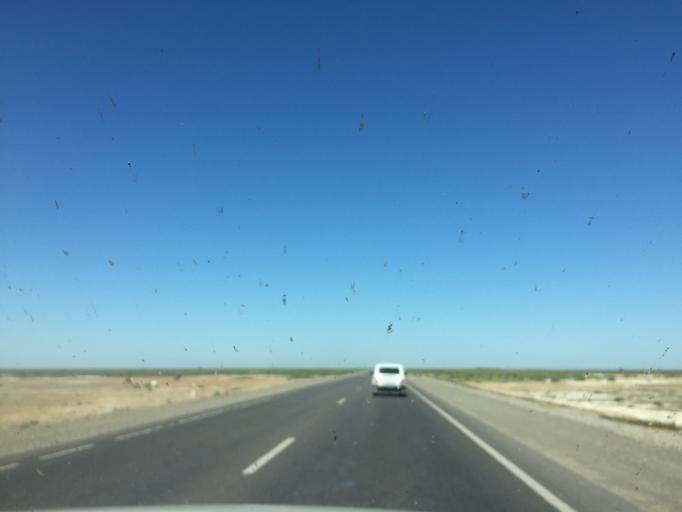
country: KZ
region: Qyzylorda
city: Kyzyl-Orda
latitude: 44.8851
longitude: 65.2607
